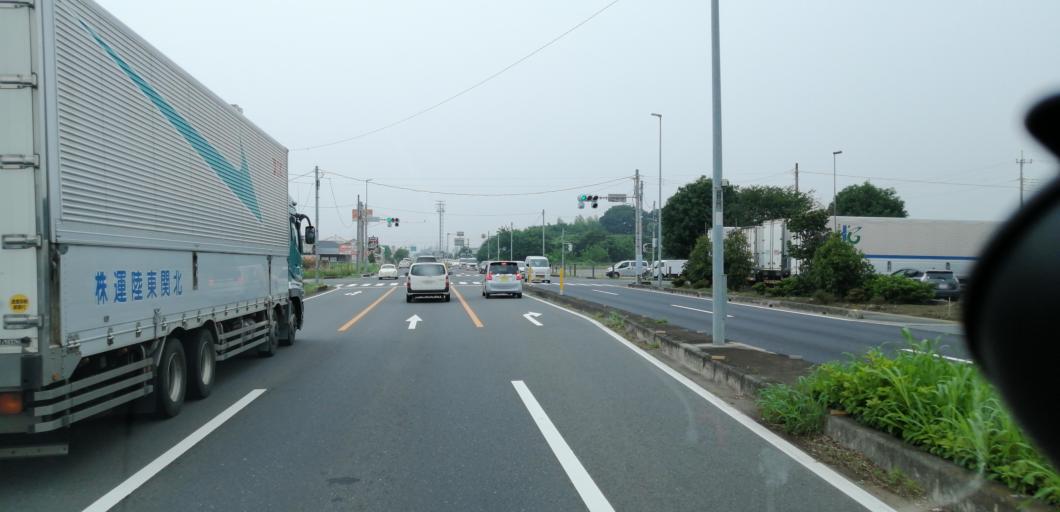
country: JP
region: Saitama
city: Fukayacho
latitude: 36.1511
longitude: 139.2887
